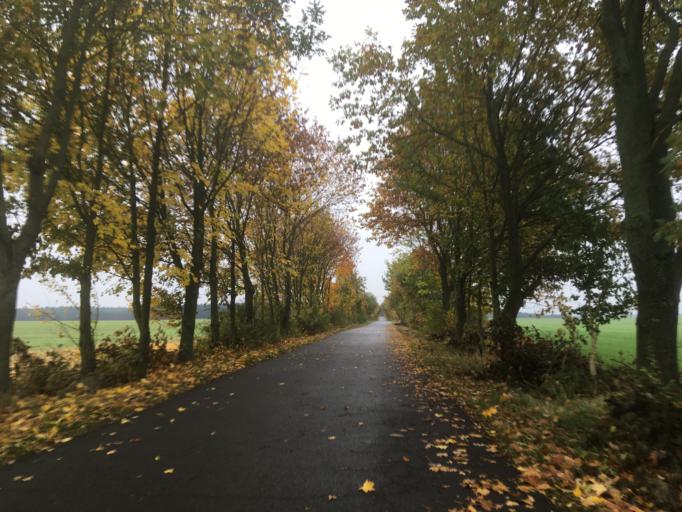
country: DE
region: Brandenburg
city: Neu Zauche
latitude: 52.0273
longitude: 14.1178
